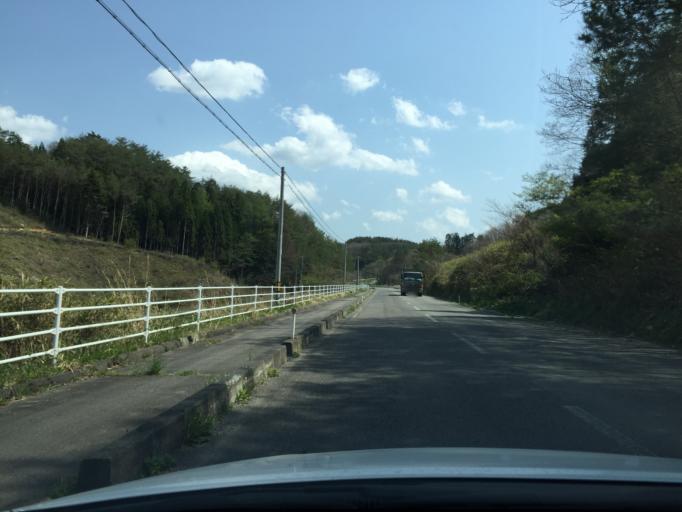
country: JP
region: Fukushima
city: Namie
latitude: 37.4035
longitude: 140.7993
